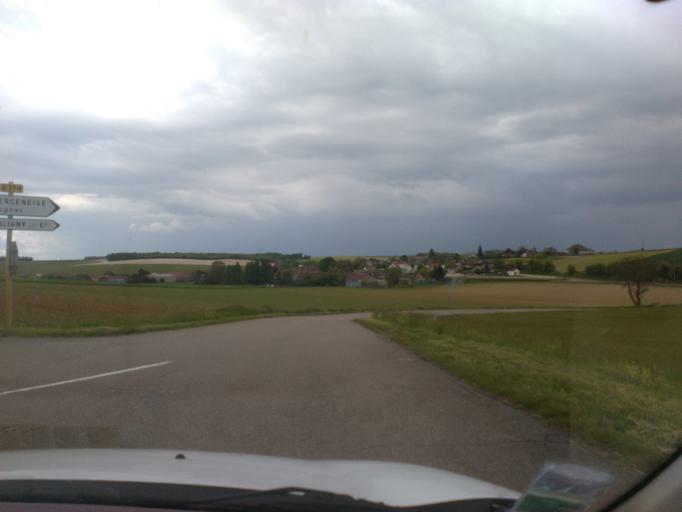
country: FR
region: Bourgogne
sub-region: Departement de l'Yonne
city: Thorigny-sur-Oreuse
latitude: 48.3614
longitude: 3.4485
